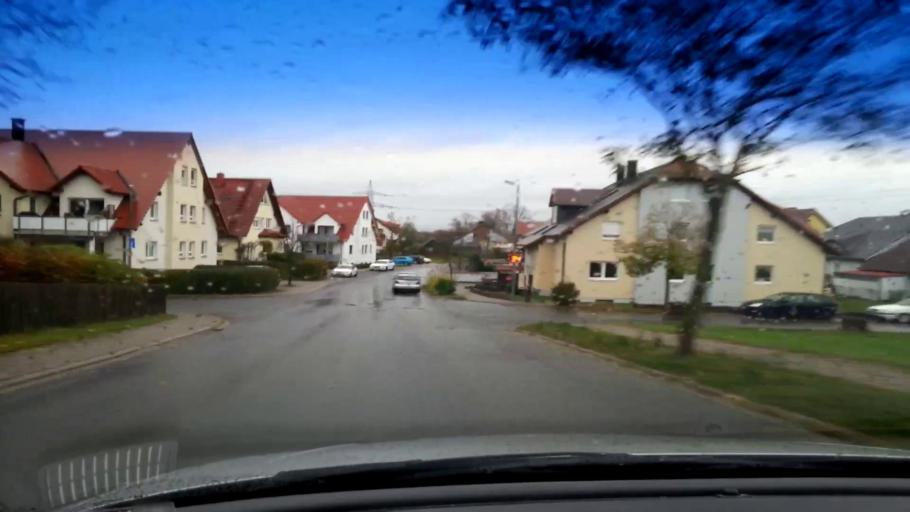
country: DE
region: Bavaria
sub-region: Upper Franconia
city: Hallstadt
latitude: 49.9327
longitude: 10.8628
